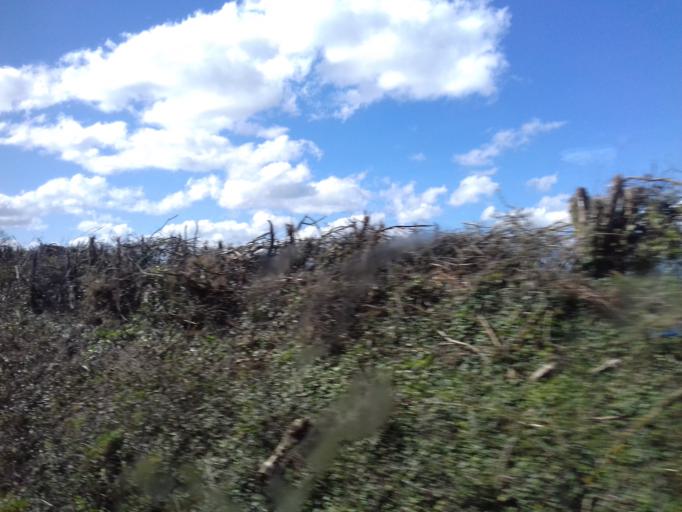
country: IE
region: Munster
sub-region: County Cork
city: Kanturk
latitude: 52.1193
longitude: -8.7791
